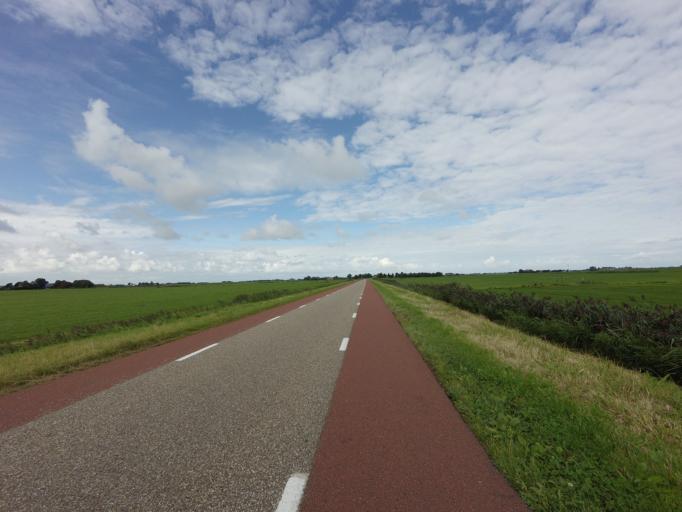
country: NL
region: Friesland
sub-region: Sudwest Fryslan
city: Workum
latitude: 53.0244
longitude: 5.4785
